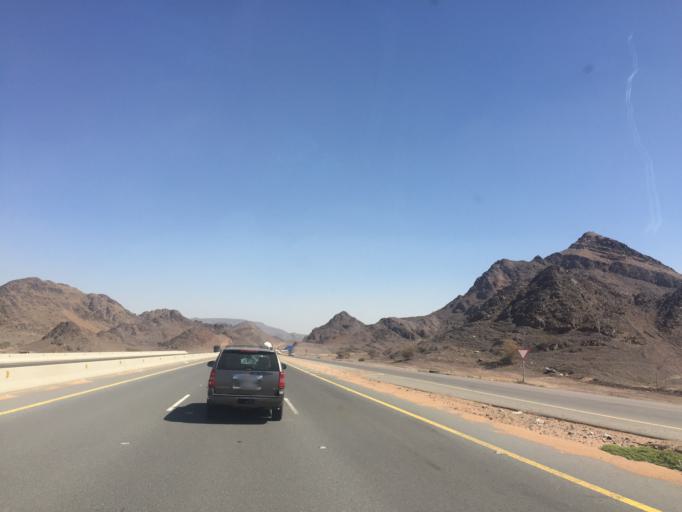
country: SA
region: Al Madinah al Munawwarah
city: Sultanah
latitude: 24.3164
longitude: 39.4303
